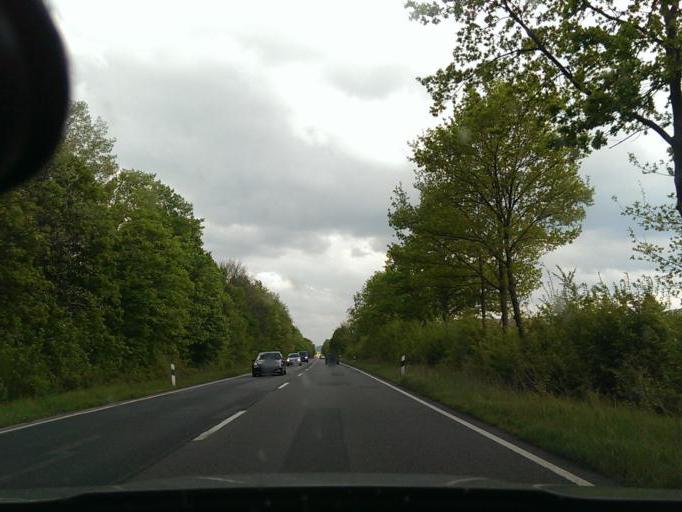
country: DE
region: Lower Saxony
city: Banteln
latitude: 52.0730
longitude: 9.7453
